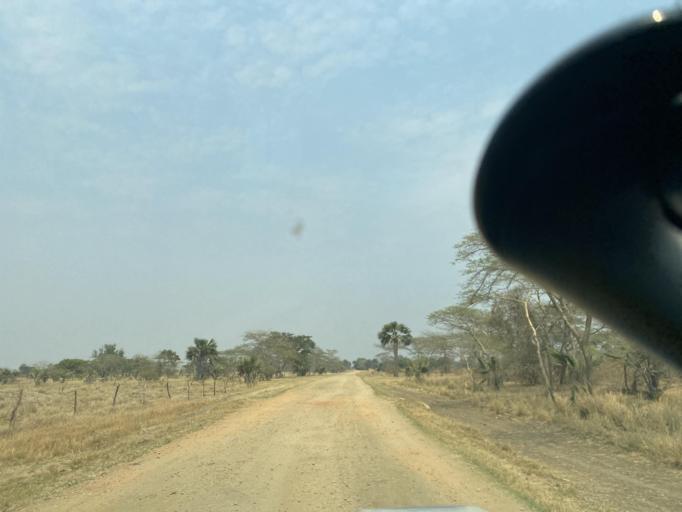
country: ZM
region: Lusaka
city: Kafue
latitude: -15.6480
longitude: 28.0384
